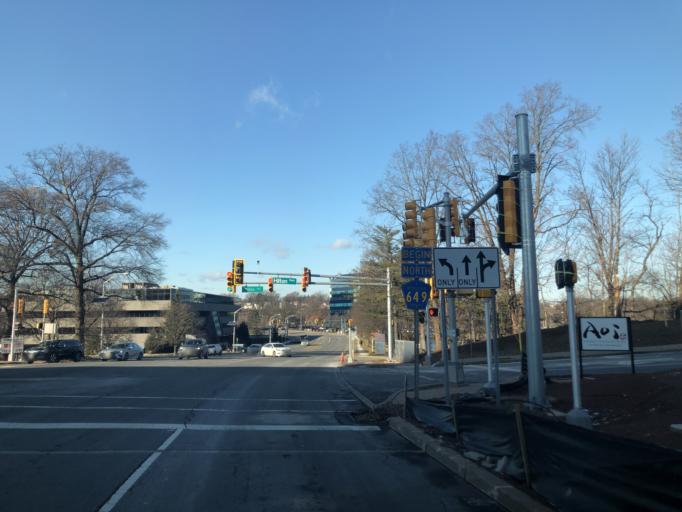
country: US
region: New Jersey
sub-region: Middlesex County
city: Iselin
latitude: 40.5620
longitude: -74.3279
